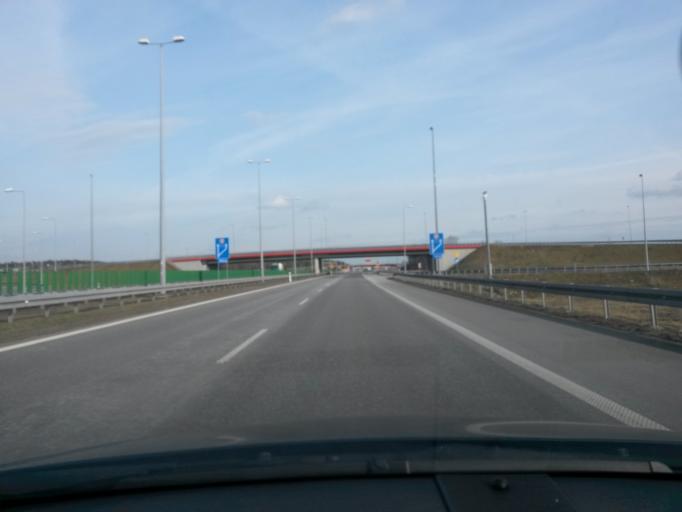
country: PL
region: Greater Poland Voivodeship
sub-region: Powiat koninski
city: Stare Miasto
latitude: 52.1565
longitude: 18.2642
